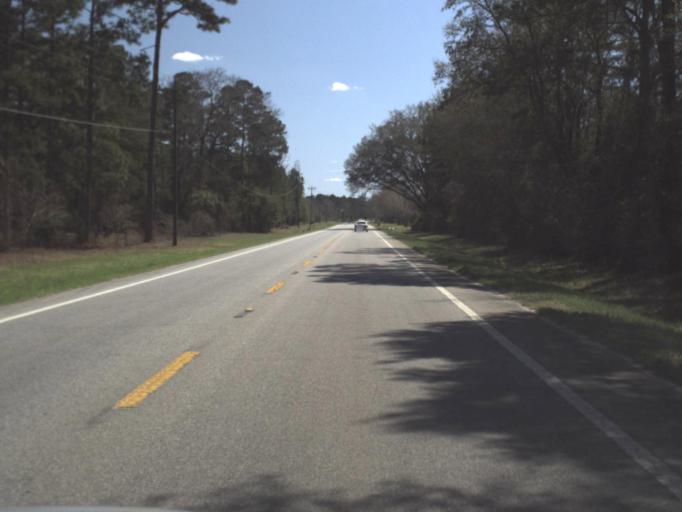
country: US
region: Florida
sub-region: Gadsden County
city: Gretna
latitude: 30.6667
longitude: -84.6112
